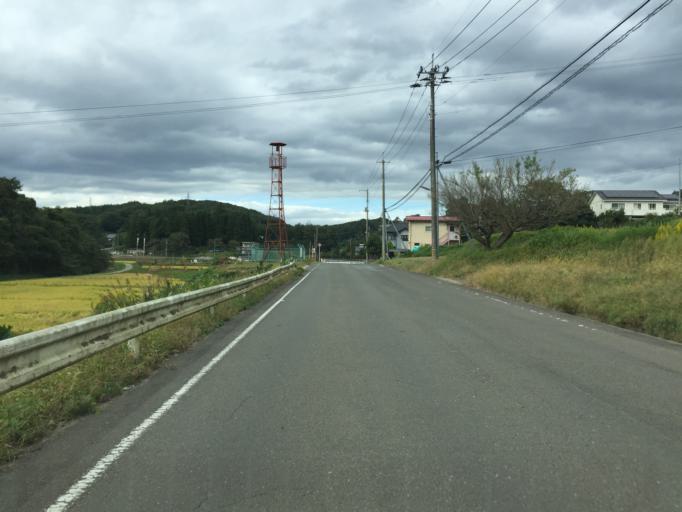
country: JP
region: Fukushima
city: Fukushima-shi
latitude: 37.6999
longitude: 140.4887
